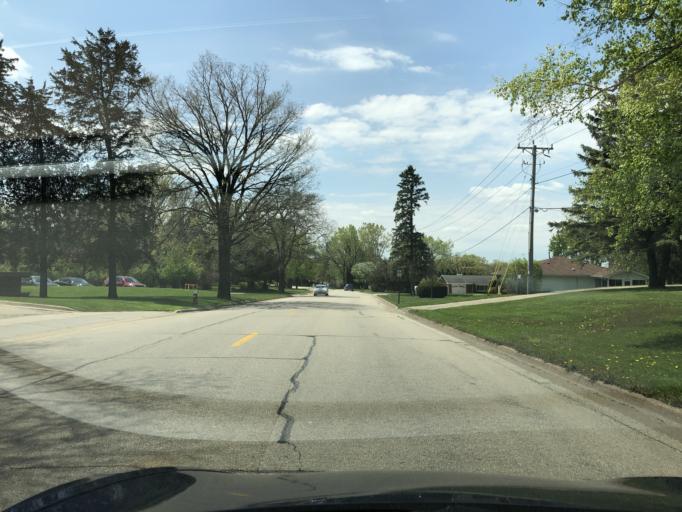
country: US
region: Iowa
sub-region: Dubuque County
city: Dubuque
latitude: 42.4756
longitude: -90.6694
